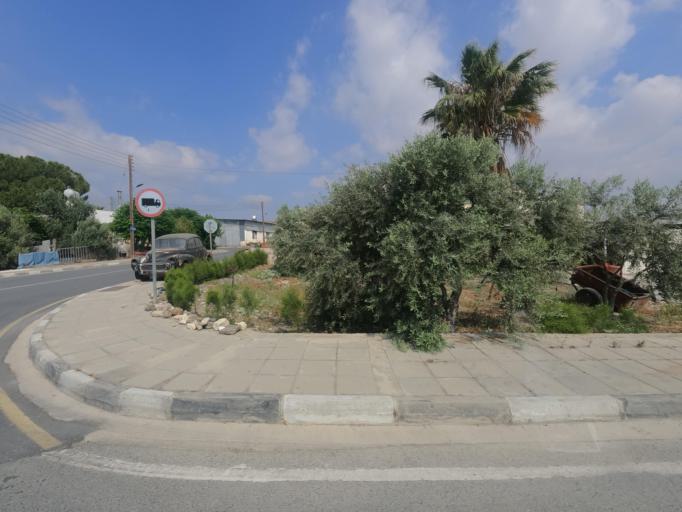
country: CY
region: Larnaka
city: Aradippou
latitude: 34.9299
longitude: 33.5426
